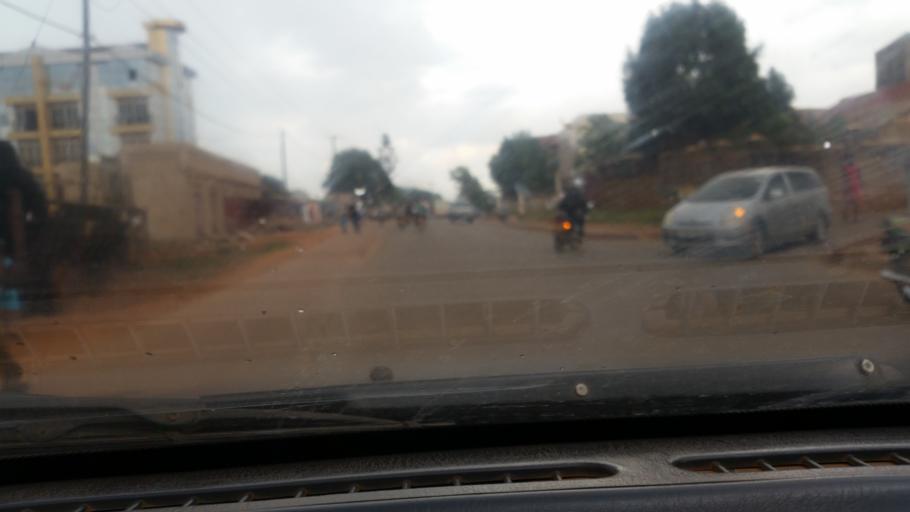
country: UG
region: Central Region
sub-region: Wakiso District
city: Kireka
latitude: 0.3564
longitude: 32.6500
